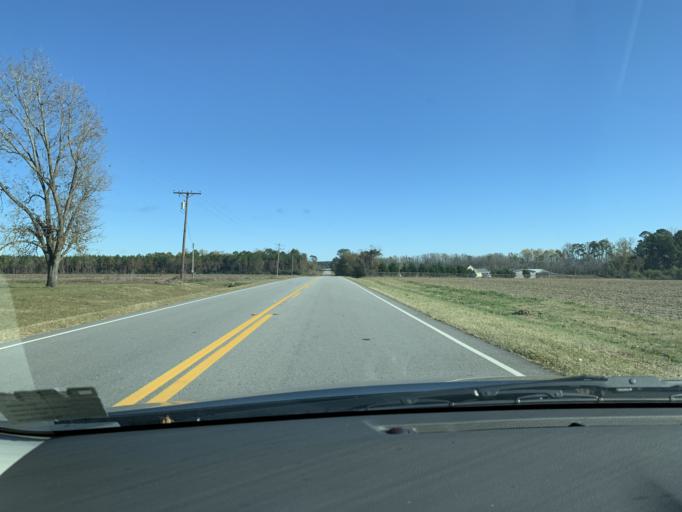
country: US
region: Georgia
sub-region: Ben Hill County
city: Fitzgerald
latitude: 31.7158
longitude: -83.1885
